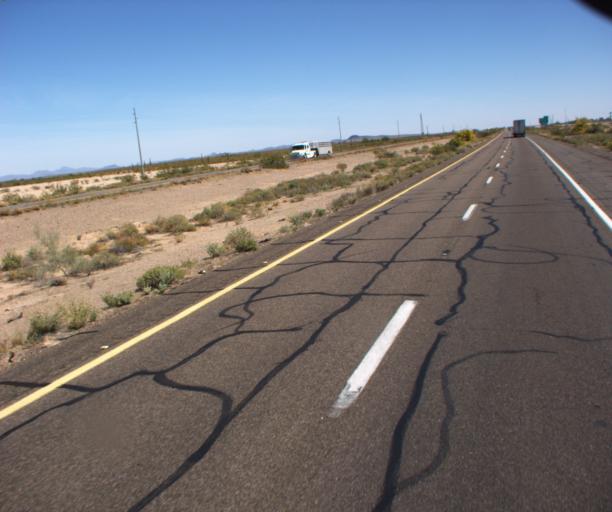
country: US
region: Arizona
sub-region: Maricopa County
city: Gila Bend
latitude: 32.8566
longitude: -113.2296
